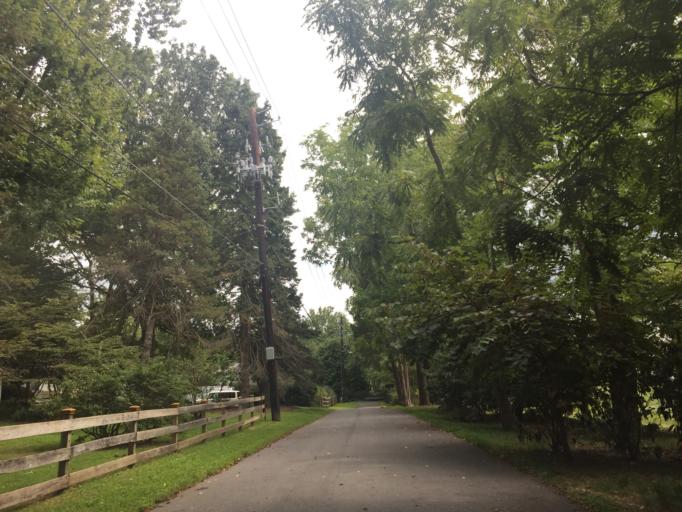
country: US
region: Maryland
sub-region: Montgomery County
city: Derwood
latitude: 39.1381
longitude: -77.1668
